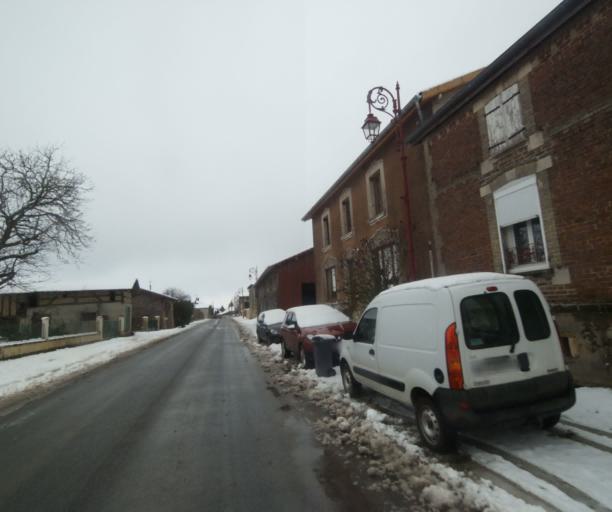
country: FR
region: Champagne-Ardenne
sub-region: Departement de la Haute-Marne
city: Laneuville-a-Remy
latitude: 48.4619
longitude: 4.8458
